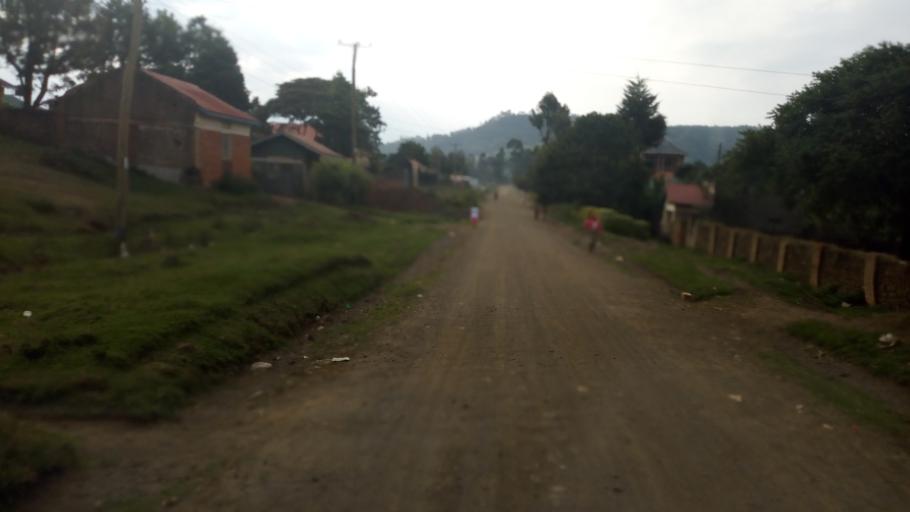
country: UG
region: Western Region
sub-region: Kisoro District
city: Kisoro
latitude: -1.2893
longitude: 29.6917
